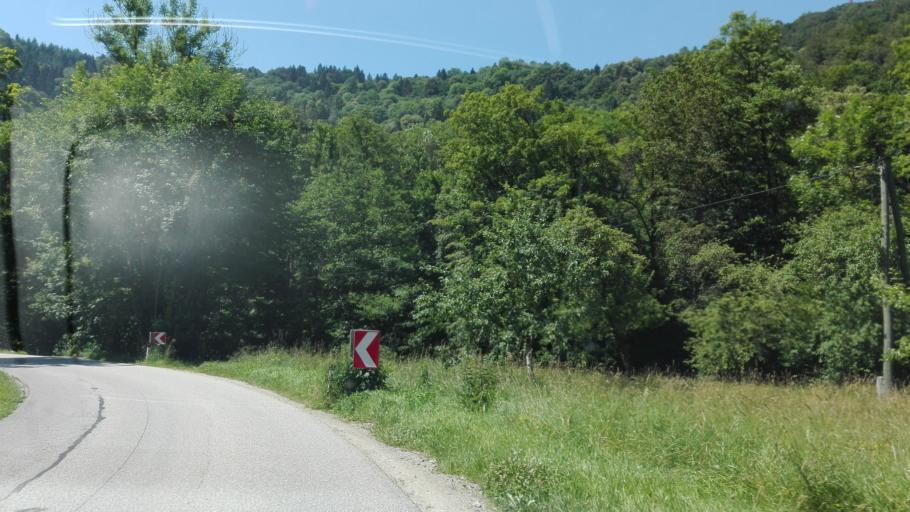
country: AT
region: Upper Austria
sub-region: Politischer Bezirk Rohrbach
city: Kleinzell im Muehlkreis
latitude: 48.3892
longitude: 13.9189
